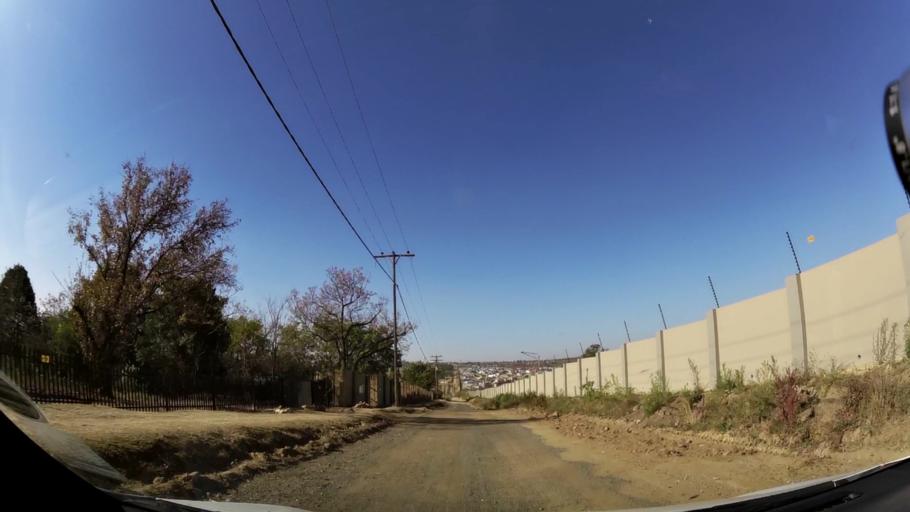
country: ZA
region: Gauteng
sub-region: City of Johannesburg Metropolitan Municipality
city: Diepsloot
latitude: -26.0086
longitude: 27.9626
